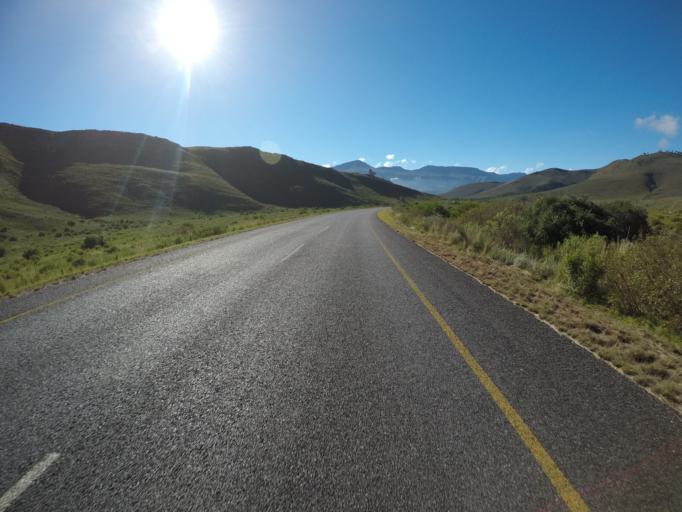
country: ZA
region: Western Cape
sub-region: Overberg District Municipality
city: Caledon
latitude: -34.0826
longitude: 19.5528
